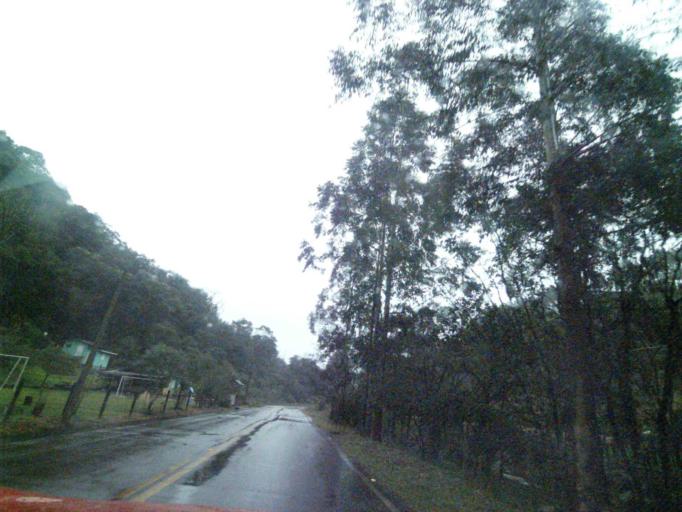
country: BR
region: Santa Catarina
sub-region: Anitapolis
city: Anitapolis
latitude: -27.8178
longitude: -49.0484
